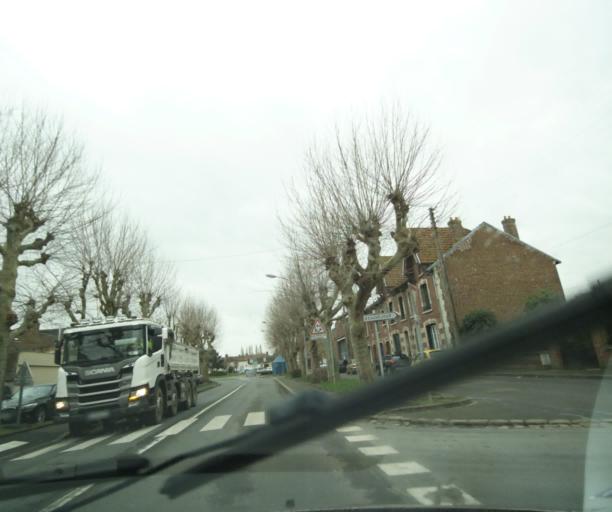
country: FR
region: Picardie
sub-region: Departement de l'Oise
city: Noyon
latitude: 49.5794
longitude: 2.9947
